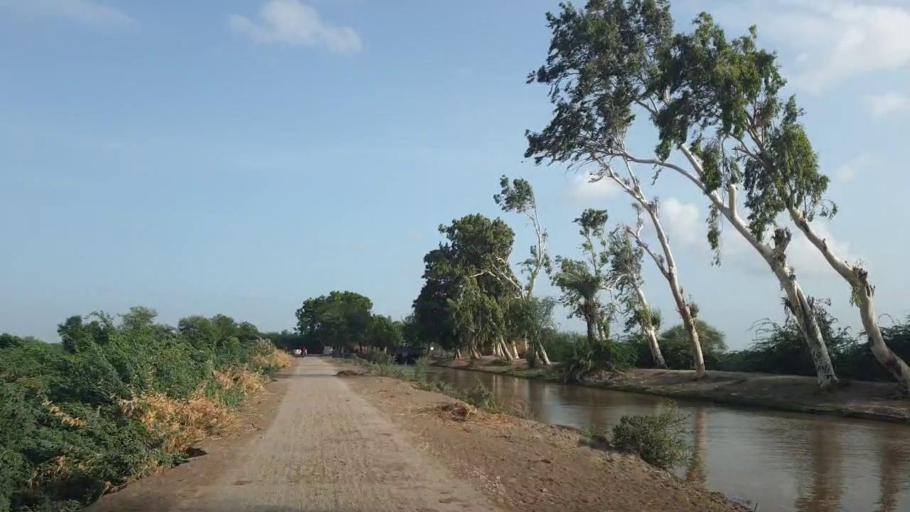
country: PK
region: Sindh
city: Kadhan
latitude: 24.6403
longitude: 69.1037
